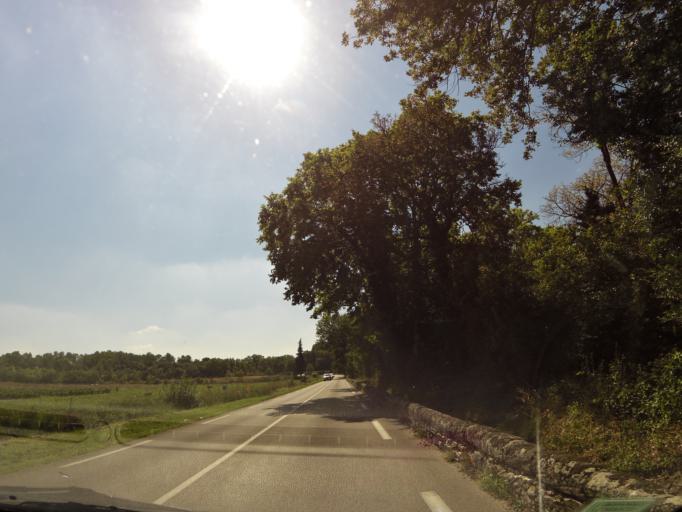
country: FR
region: Languedoc-Roussillon
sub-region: Departement du Gard
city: Villevieille
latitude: 43.8107
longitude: 4.0942
